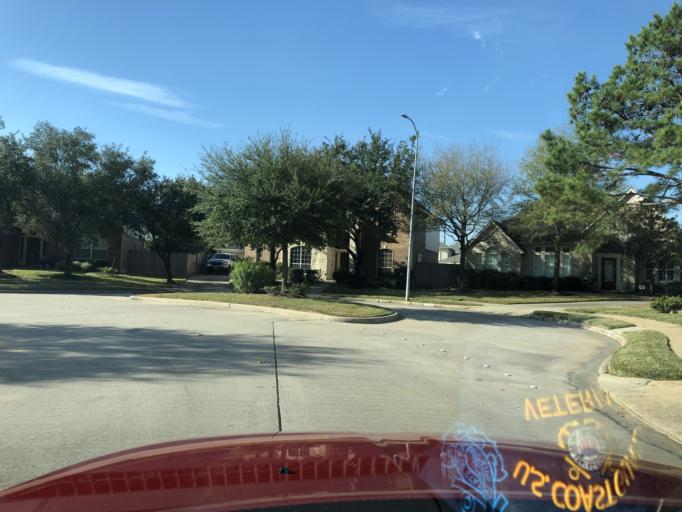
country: US
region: Texas
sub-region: Harris County
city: Tomball
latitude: 30.0316
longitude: -95.5636
